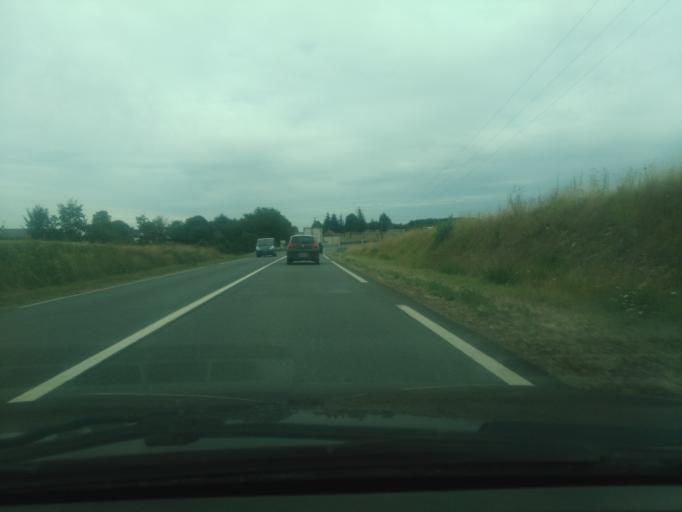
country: FR
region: Poitou-Charentes
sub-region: Departement de la Vienne
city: Saint-Savin
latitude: 46.5680
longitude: 0.8496
